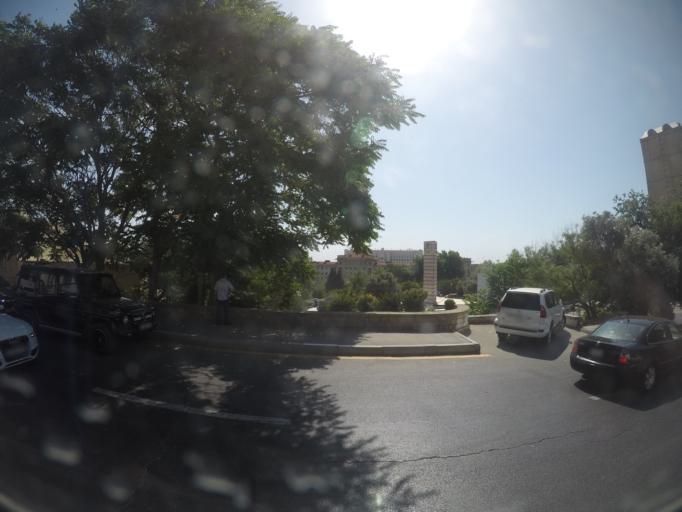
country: AZ
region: Baki
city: Badamdar
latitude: 40.3642
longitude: 49.8262
